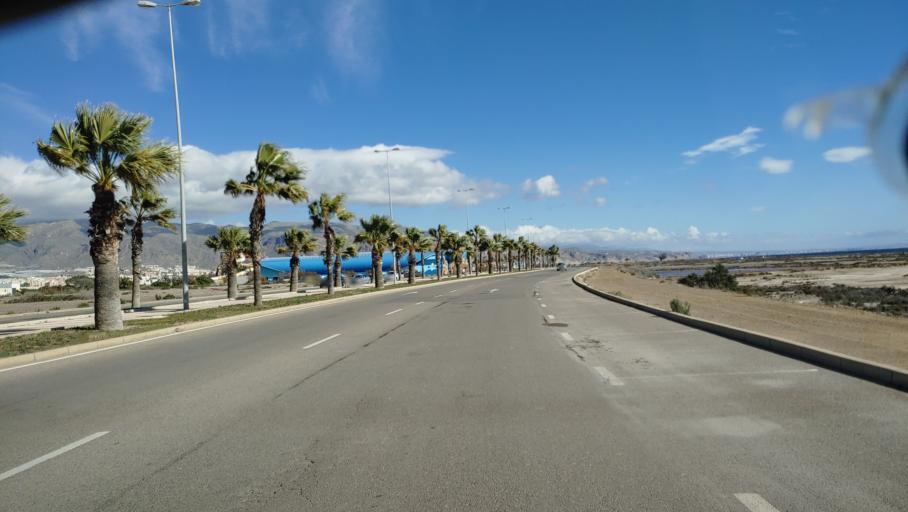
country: ES
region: Andalusia
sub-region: Provincia de Almeria
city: Roquetas de Mar
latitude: 36.7795
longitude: -2.6061
